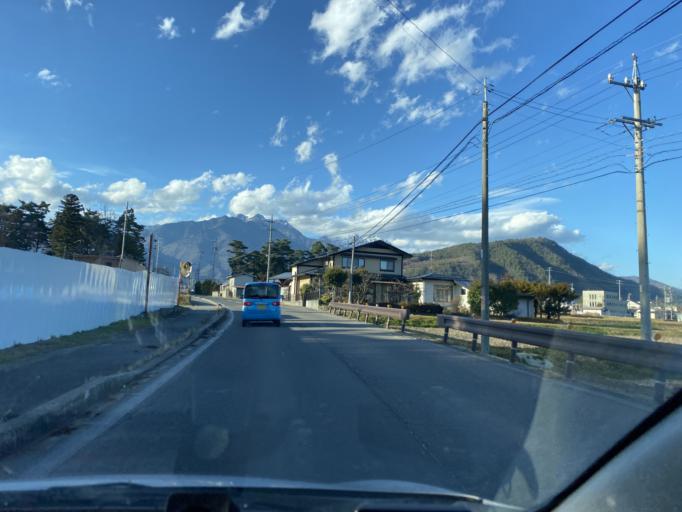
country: JP
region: Nagano
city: Omachi
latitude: 36.5213
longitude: 137.8357
